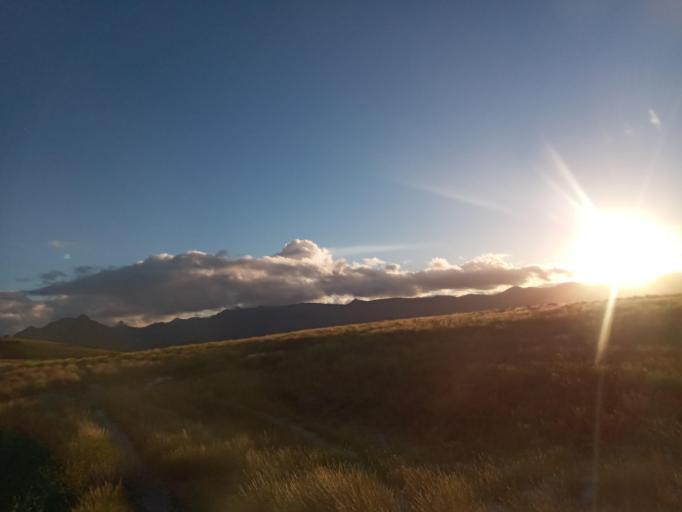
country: MG
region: Anosy
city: Fort Dauphin
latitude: -24.5117
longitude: 47.2558
